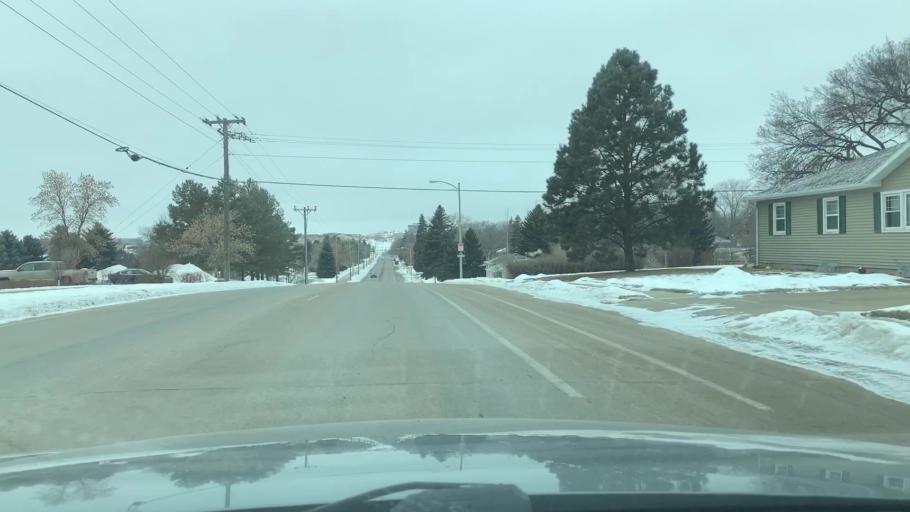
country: US
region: North Dakota
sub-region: Burleigh County
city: Bismarck
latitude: 46.8237
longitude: -100.7969
